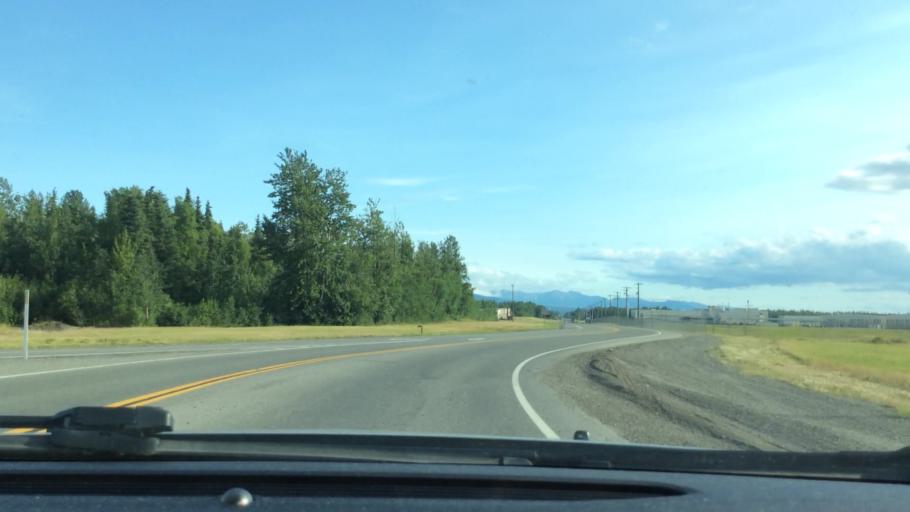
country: US
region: Alaska
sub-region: Anchorage Municipality
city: Anchorage
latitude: 61.2524
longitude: -149.7784
